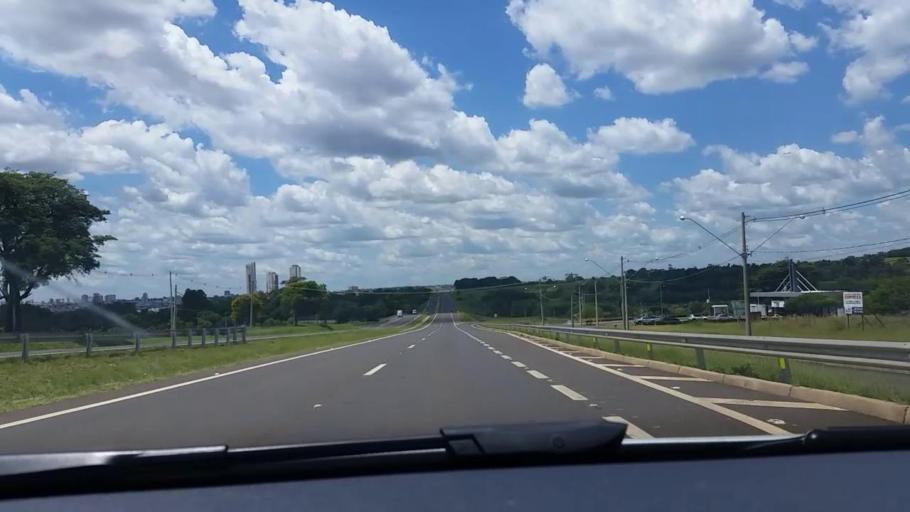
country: BR
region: Sao Paulo
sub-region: Bauru
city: Bauru
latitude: -22.3885
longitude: -49.0749
